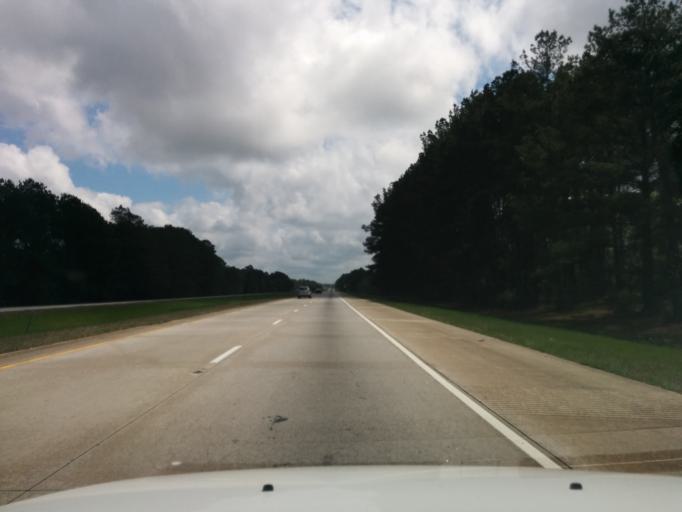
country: US
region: Georgia
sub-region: Bulloch County
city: Brooklet
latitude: 32.2741
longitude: -81.7539
